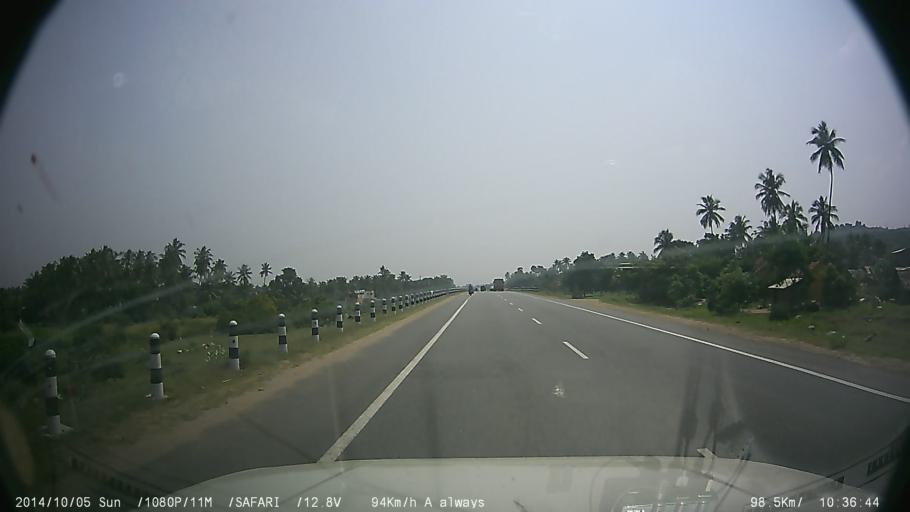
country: IN
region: Tamil Nadu
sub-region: Salem
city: Salem
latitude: 11.6604
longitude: 78.2194
